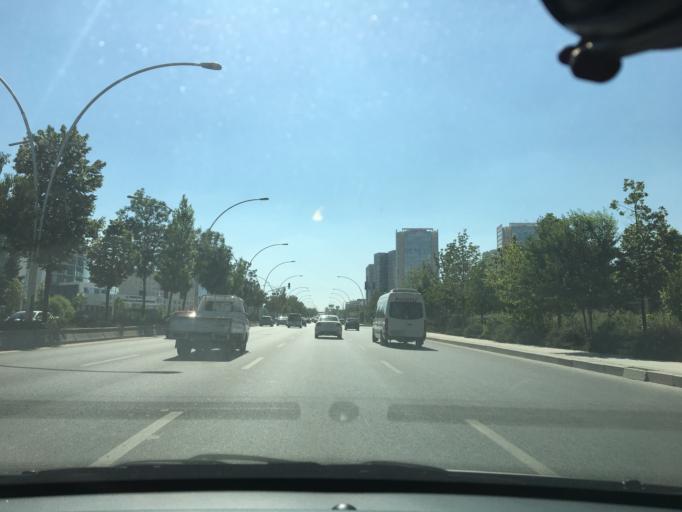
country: TR
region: Ankara
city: Batikent
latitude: 39.9078
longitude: 32.7613
